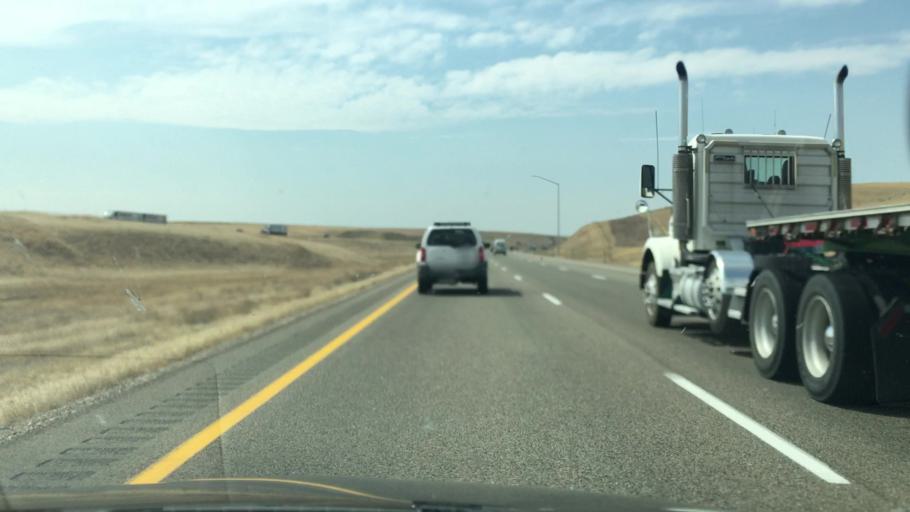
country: US
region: Idaho
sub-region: Ada County
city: Boise
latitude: 43.4851
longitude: -116.1163
